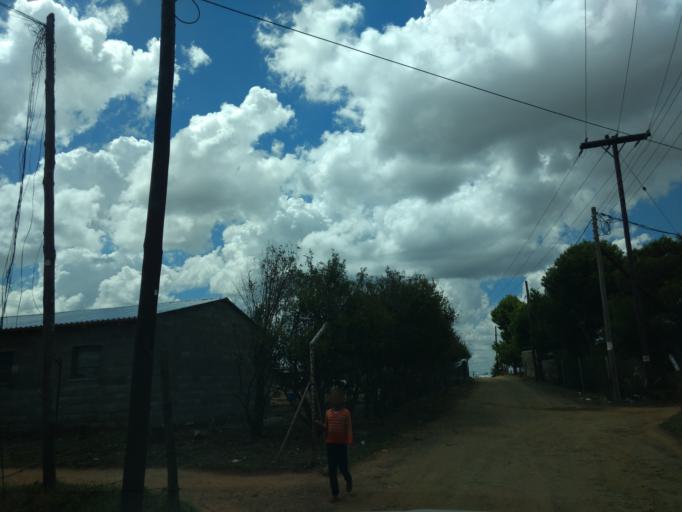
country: LS
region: Maseru
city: Maseru
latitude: -29.3692
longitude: 27.5120
